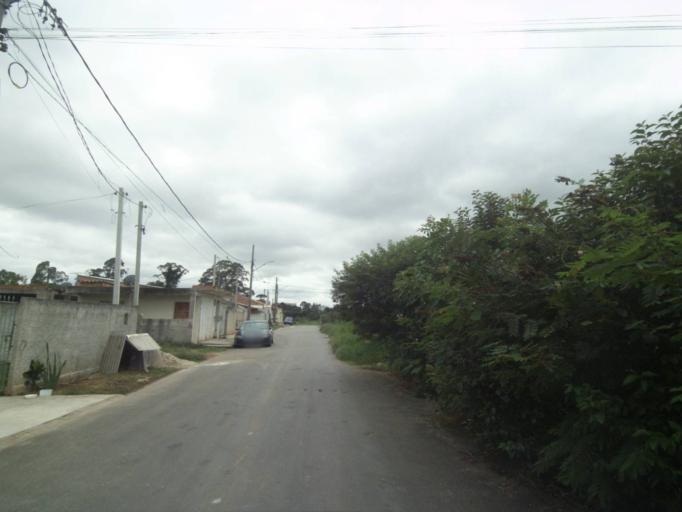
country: BR
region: Parana
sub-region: Pinhais
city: Pinhais
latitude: -25.4568
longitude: -49.1959
